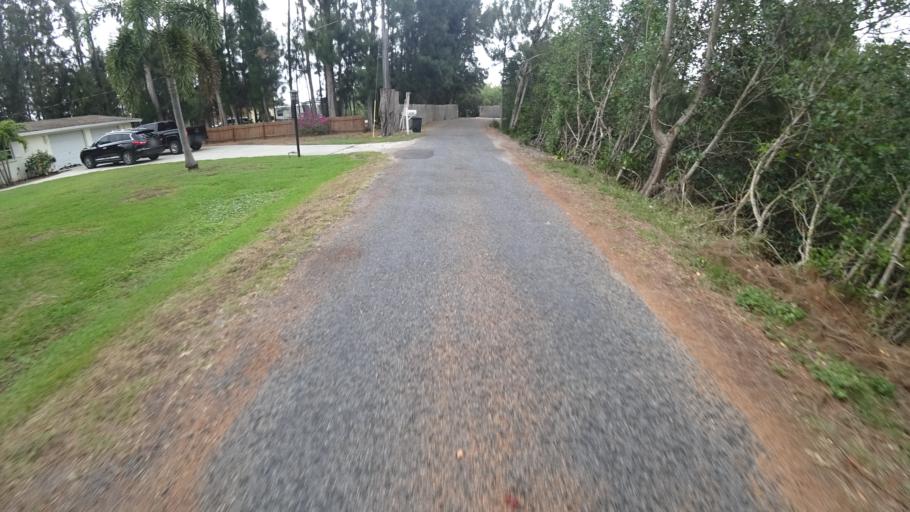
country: US
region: Florida
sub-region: Manatee County
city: Samoset
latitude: 27.4817
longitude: -82.5051
